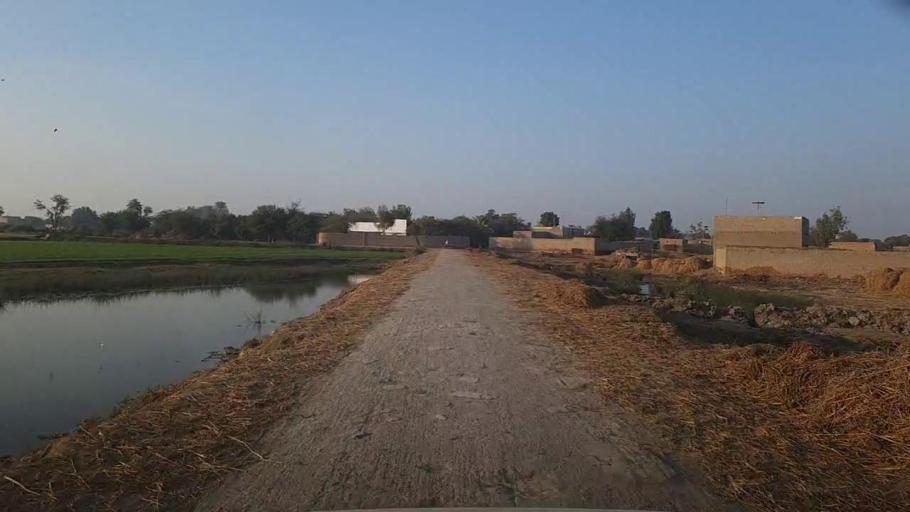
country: PK
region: Sindh
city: Mehar
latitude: 27.1974
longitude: 67.7814
